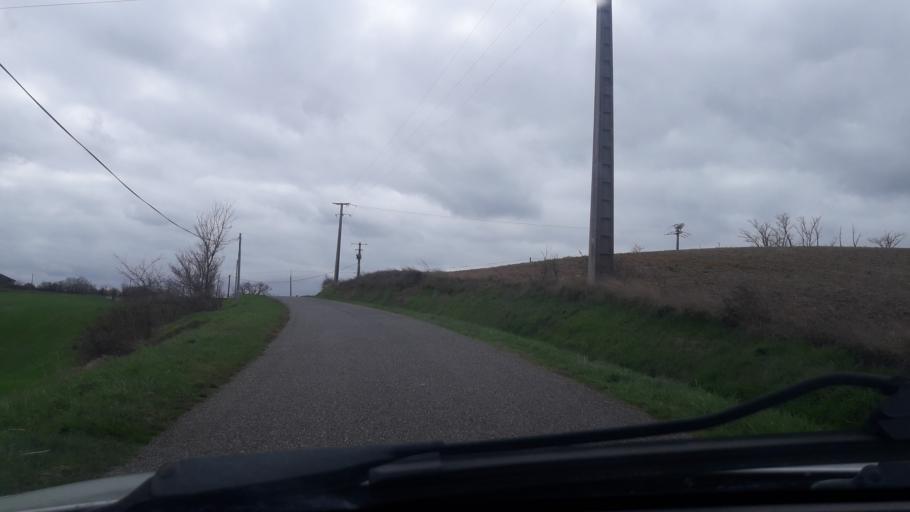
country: FR
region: Midi-Pyrenees
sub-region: Departement de la Haute-Garonne
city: Montesquieu-Volvestre
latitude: 43.2041
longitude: 1.3084
